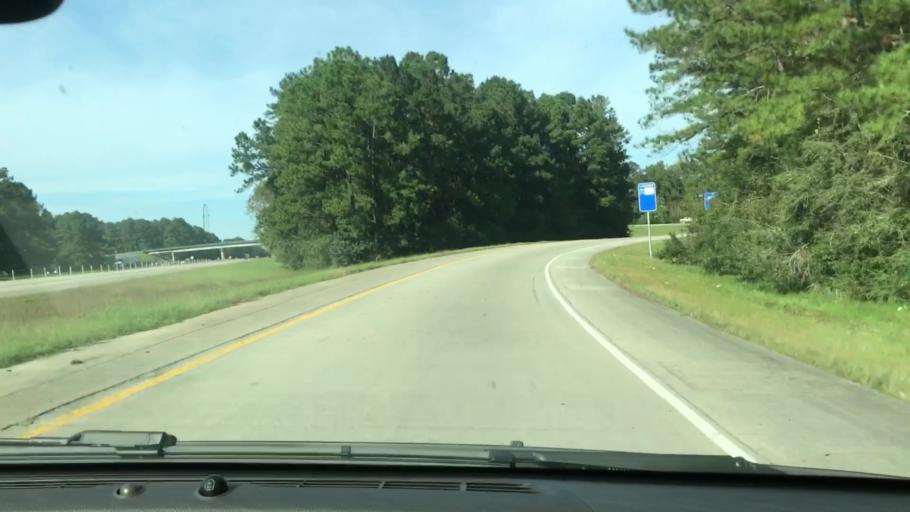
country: US
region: Louisiana
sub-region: Saint Tammany Parish
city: Pearl River
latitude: 30.3500
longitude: -89.7397
